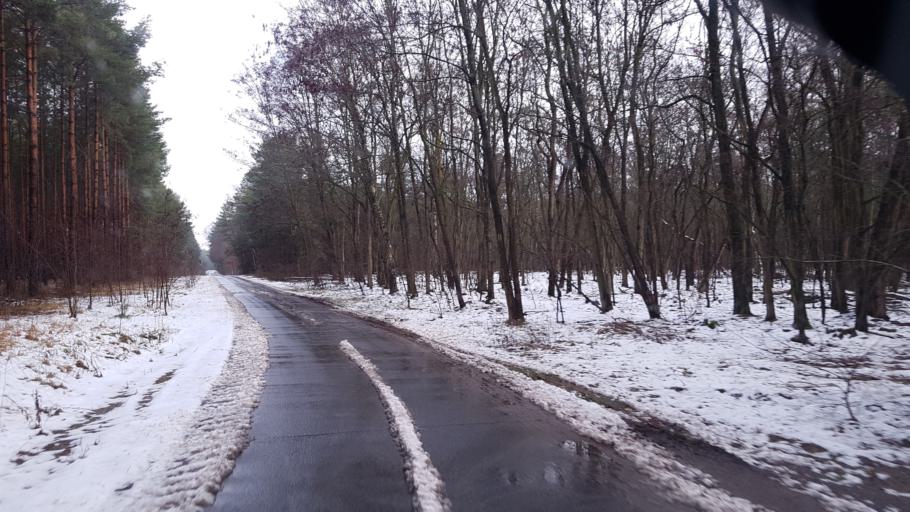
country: DE
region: Brandenburg
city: Straupitz
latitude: 51.9633
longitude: 14.1659
